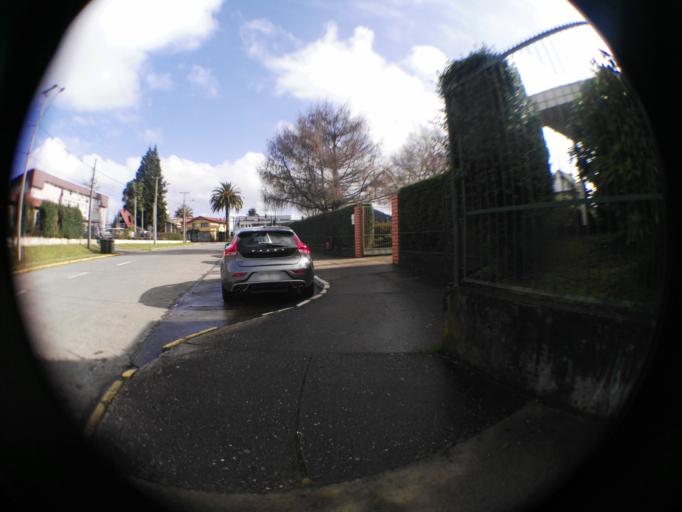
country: CL
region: Los Lagos
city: Las Animas
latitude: -39.8199
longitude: -73.2290
